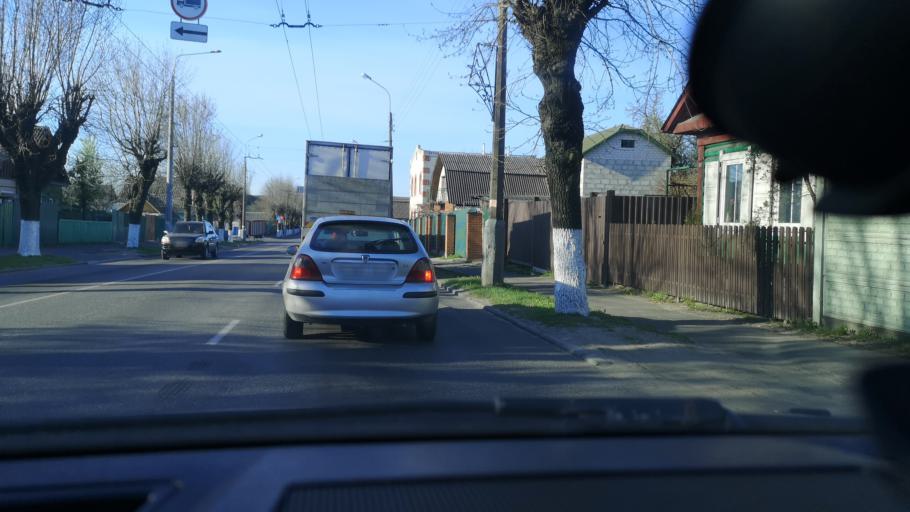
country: BY
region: Gomel
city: Gomel
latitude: 52.4269
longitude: 30.9744
